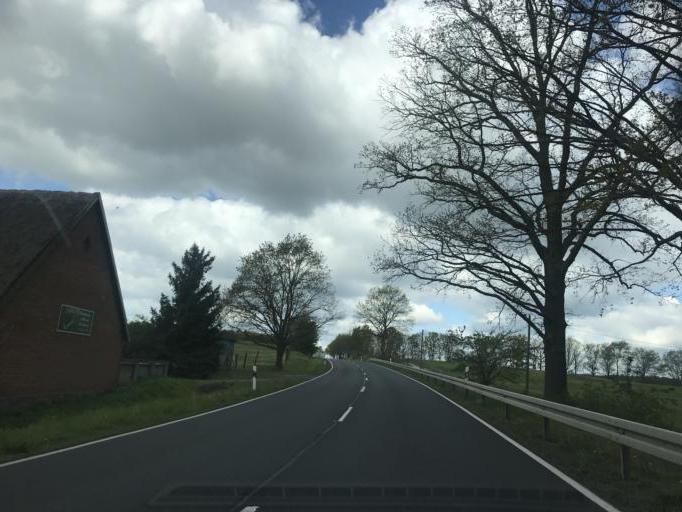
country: DE
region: Brandenburg
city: Zehdenick
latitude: 52.8996
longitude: 13.2343
